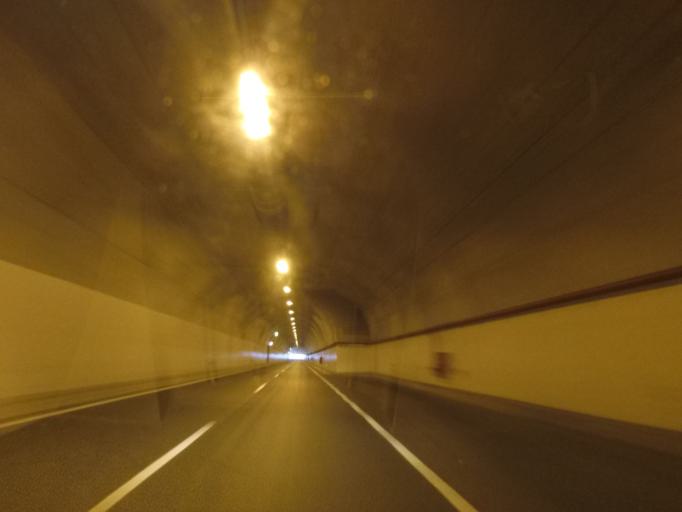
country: PT
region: Madeira
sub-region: Machico
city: Canical
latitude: 32.7404
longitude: -16.7484
